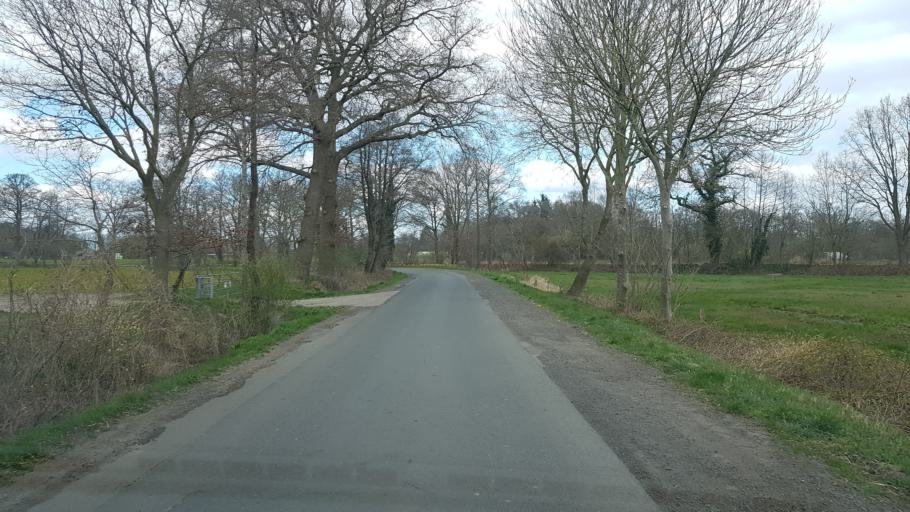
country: DE
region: Lower Saxony
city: Edewecht
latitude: 53.1127
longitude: 7.9431
